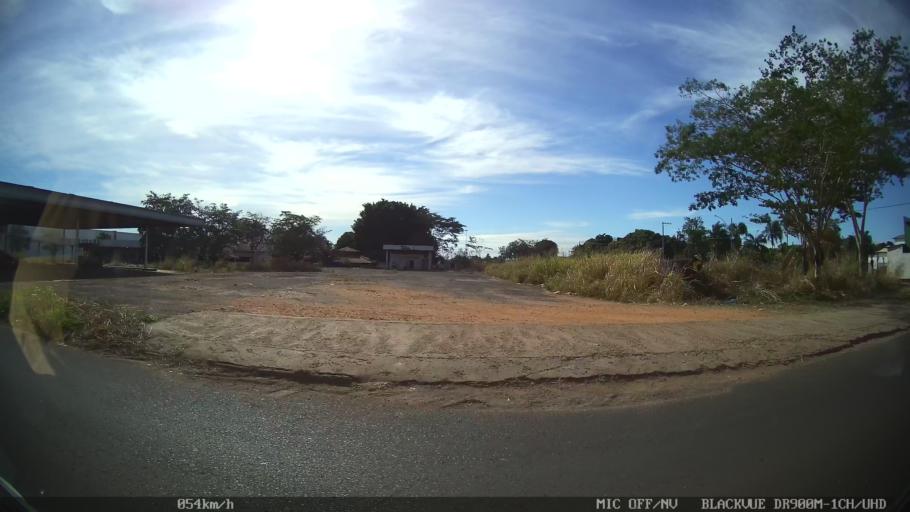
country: BR
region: Sao Paulo
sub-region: Sao Jose Do Rio Preto
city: Sao Jose do Rio Preto
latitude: -20.7926
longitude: -49.3059
